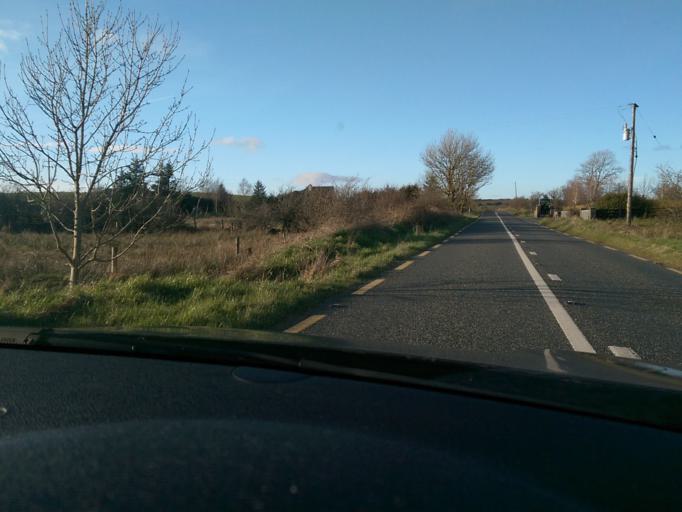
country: IE
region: Connaught
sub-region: Roscommon
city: Boyle
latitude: 53.9307
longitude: -8.2773
